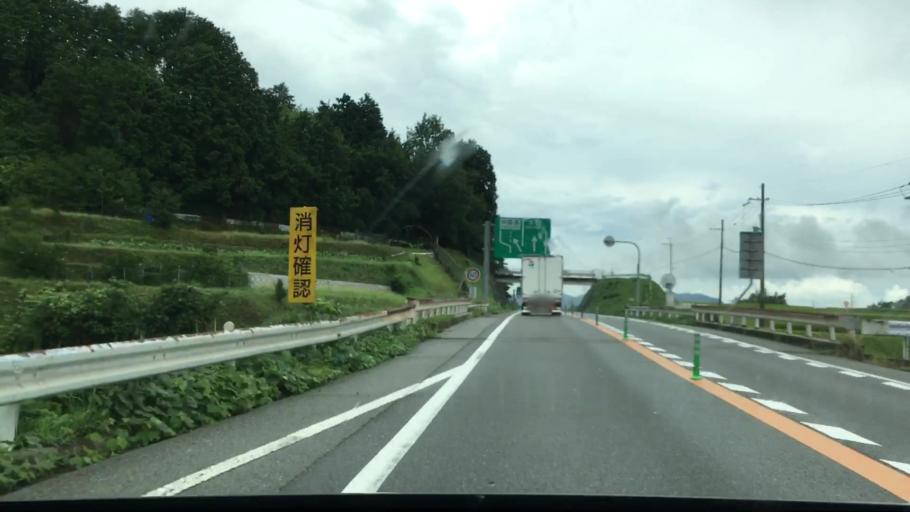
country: JP
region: Hyogo
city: Himeji
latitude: 34.9621
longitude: 134.7697
